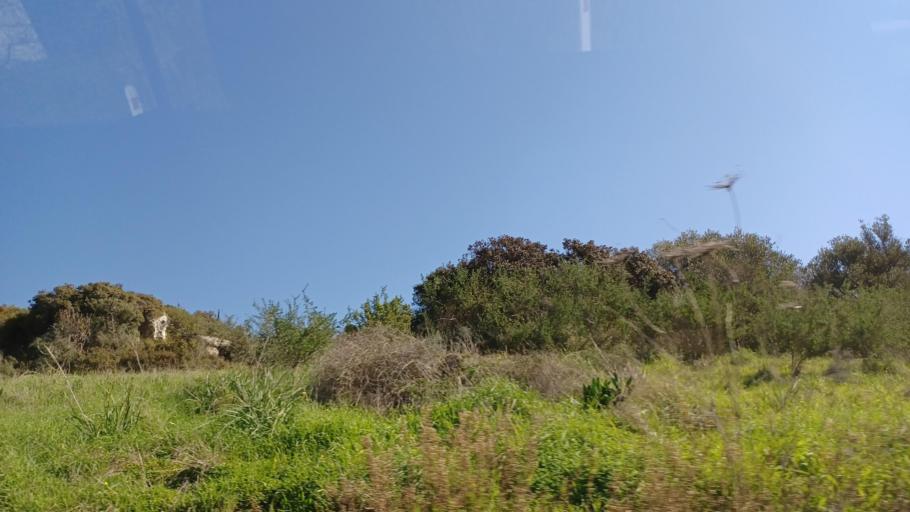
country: CY
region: Larnaka
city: Agios Tychon
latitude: 34.7285
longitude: 33.1426
